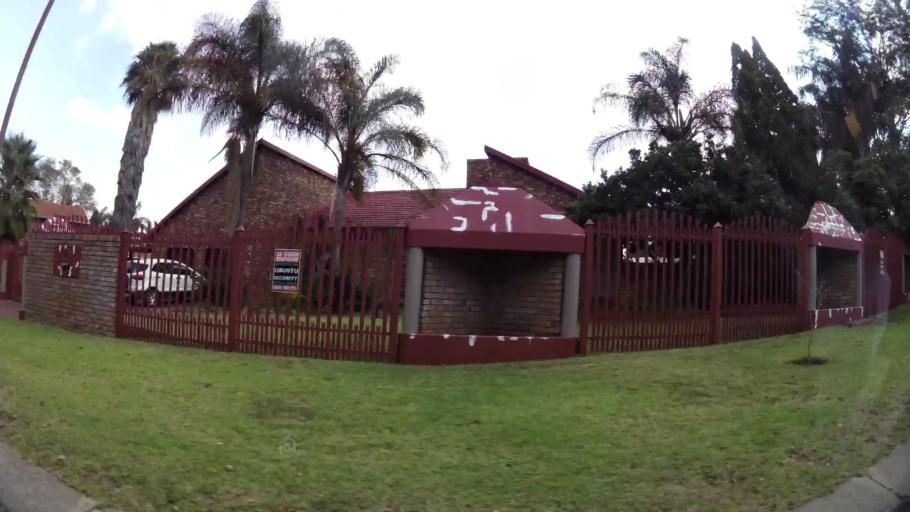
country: ZA
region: Gauteng
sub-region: City of Tshwane Metropolitan Municipality
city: Centurion
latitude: -25.8426
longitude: 28.2711
